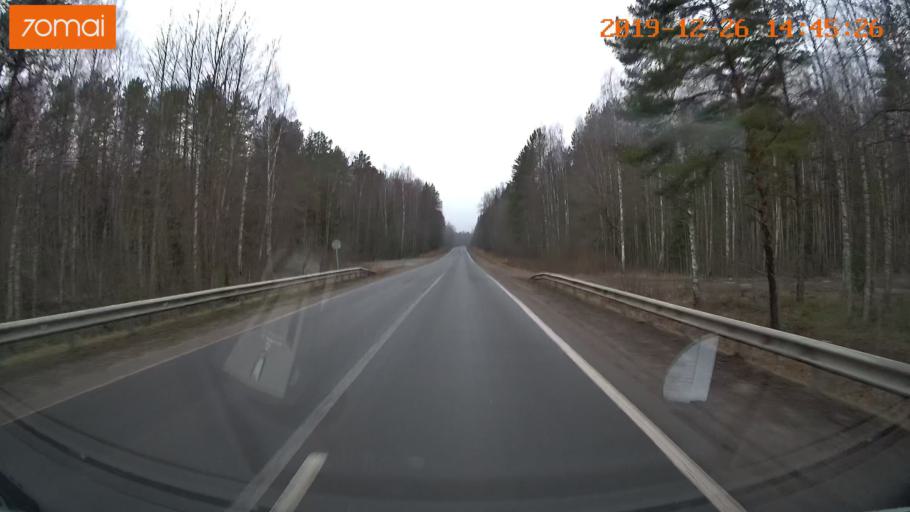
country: RU
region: Jaroslavl
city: Poshekhon'ye
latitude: 58.3382
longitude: 39.0399
